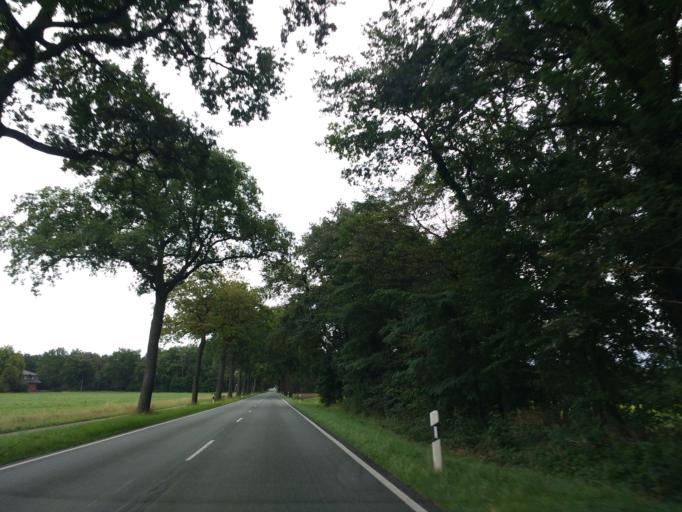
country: DE
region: Lower Saxony
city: Glandorf
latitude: 52.0903
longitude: 8.0435
